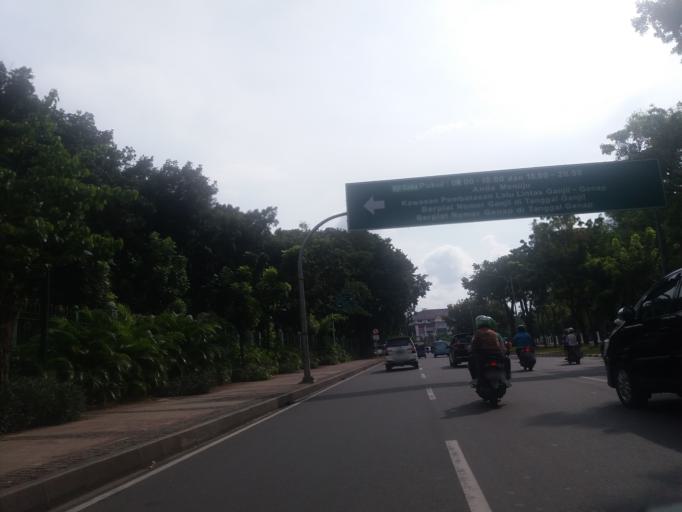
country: ID
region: Jakarta Raya
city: Jakarta
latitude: -6.1715
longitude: 106.8250
